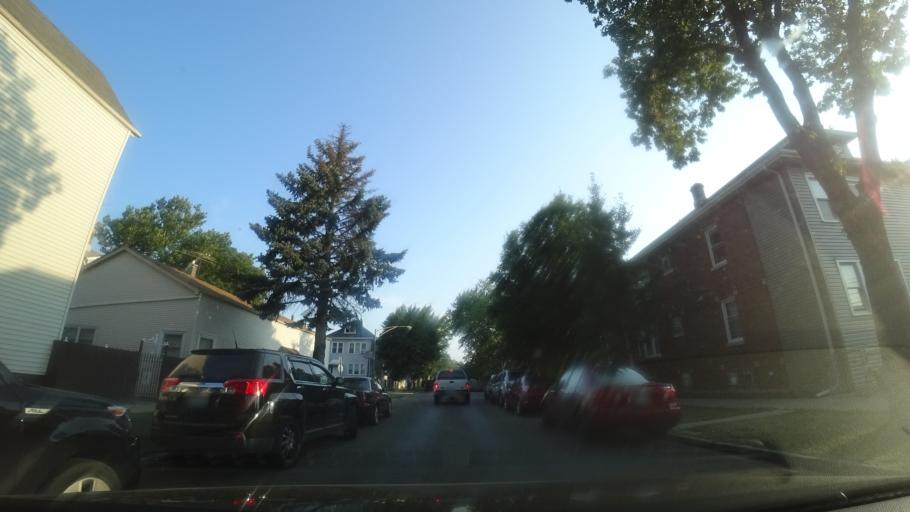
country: US
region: Illinois
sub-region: Cook County
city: Elmwood Park
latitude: 41.9272
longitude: -87.7637
